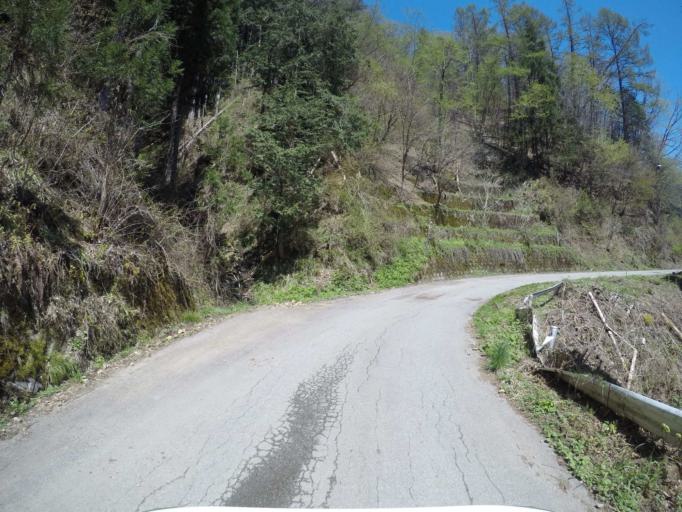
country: JP
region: Gifu
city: Takayama
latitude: 36.1659
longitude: 137.4381
